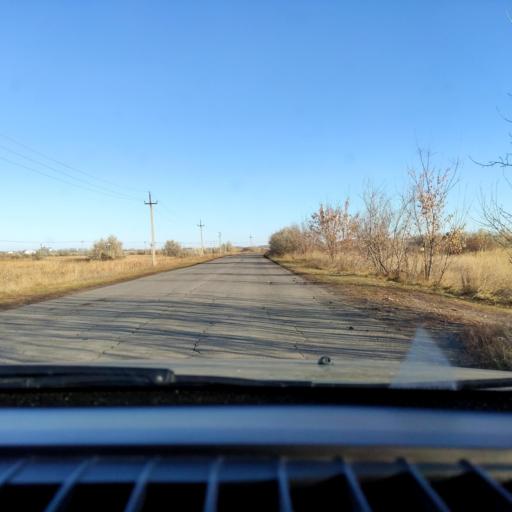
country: RU
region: Samara
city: Tol'yatti
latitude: 53.6421
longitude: 49.3154
